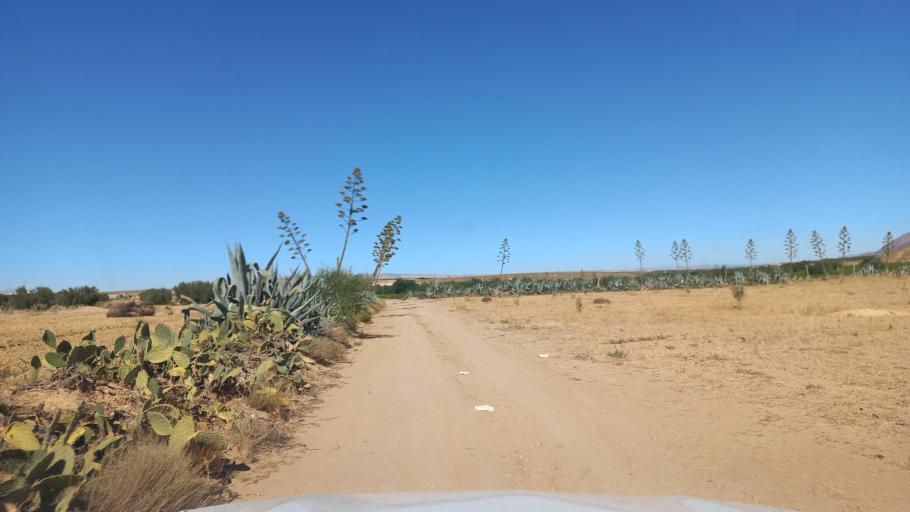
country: TN
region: Al Qasrayn
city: Sbiba
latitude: 35.4025
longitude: 9.0871
